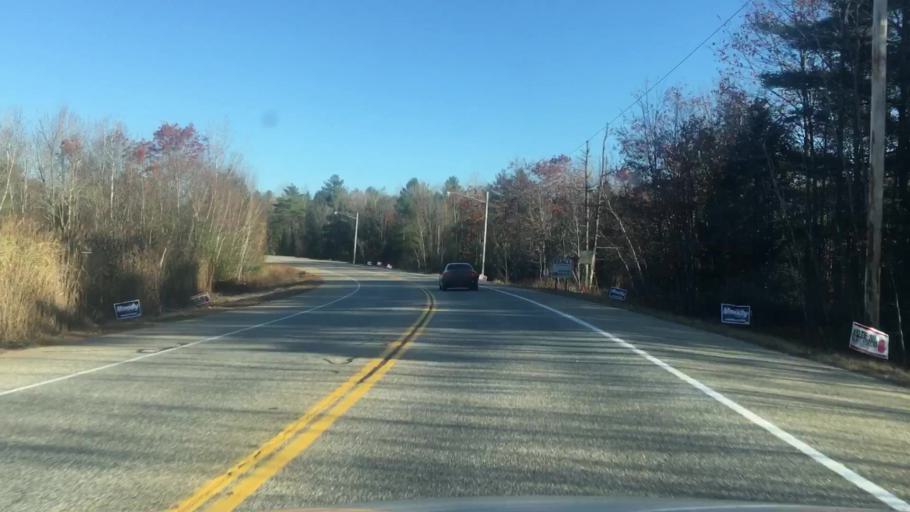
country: US
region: Maine
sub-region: Androscoggin County
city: Lewiston
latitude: 44.0784
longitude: -70.1781
